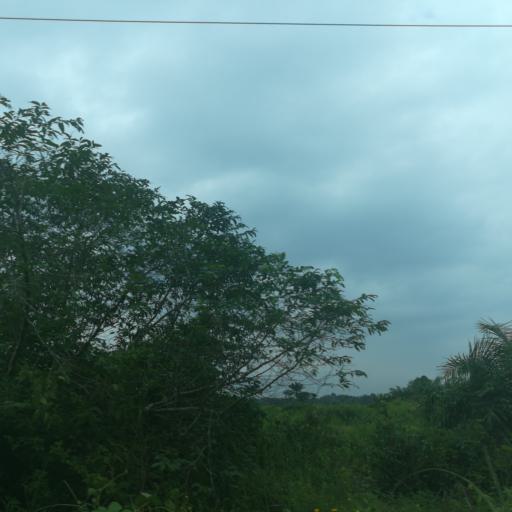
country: NG
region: Lagos
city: Ejirin
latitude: 6.6562
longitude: 3.8211
